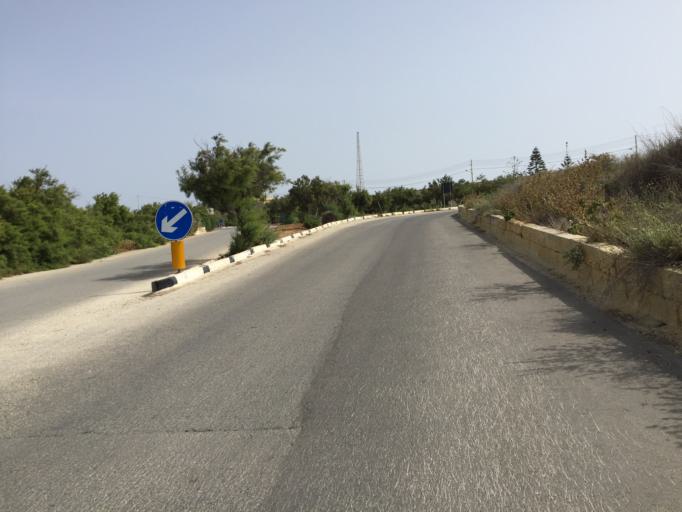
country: MT
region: Il-Kalkara
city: Kalkara
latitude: 35.8953
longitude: 14.5302
